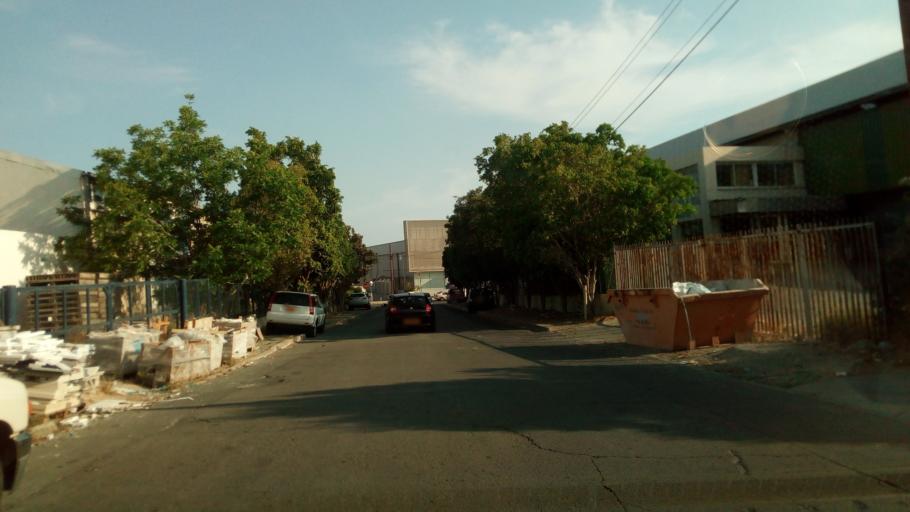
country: CY
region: Limassol
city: Limassol
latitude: 34.7040
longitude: 33.0665
